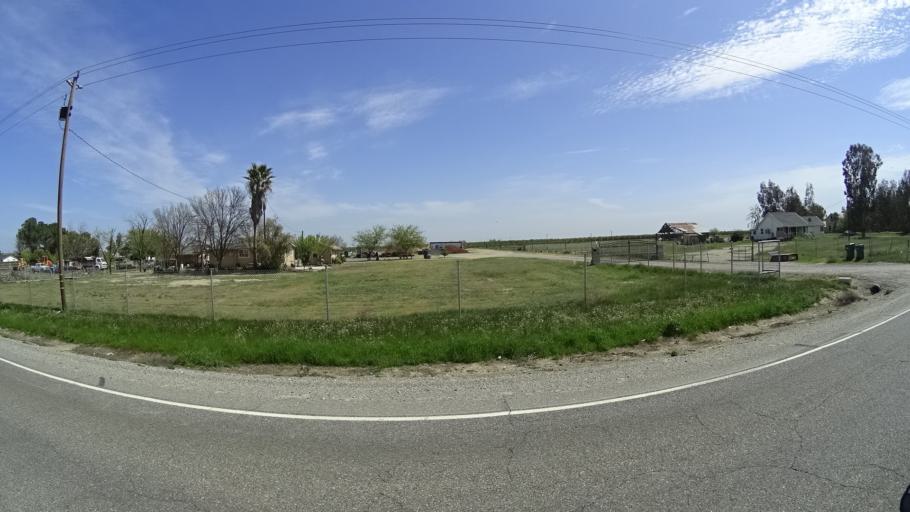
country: US
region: California
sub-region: Glenn County
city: Willows
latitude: 39.6326
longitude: -122.1974
